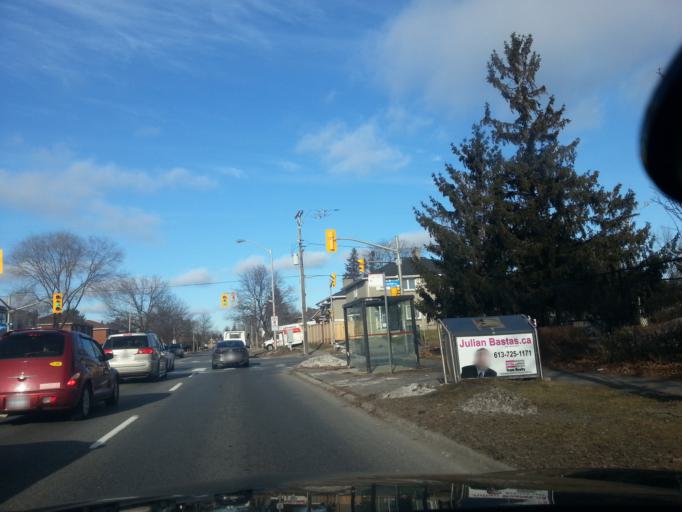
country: CA
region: Ontario
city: Bells Corners
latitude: 45.3656
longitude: -75.7707
